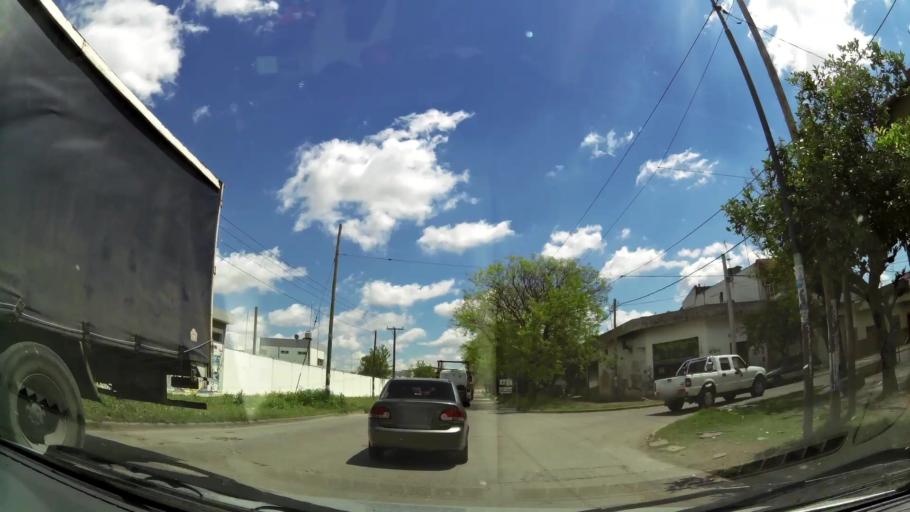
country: AR
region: Buenos Aires F.D.
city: Villa Lugano
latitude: -34.6882
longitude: -58.4379
